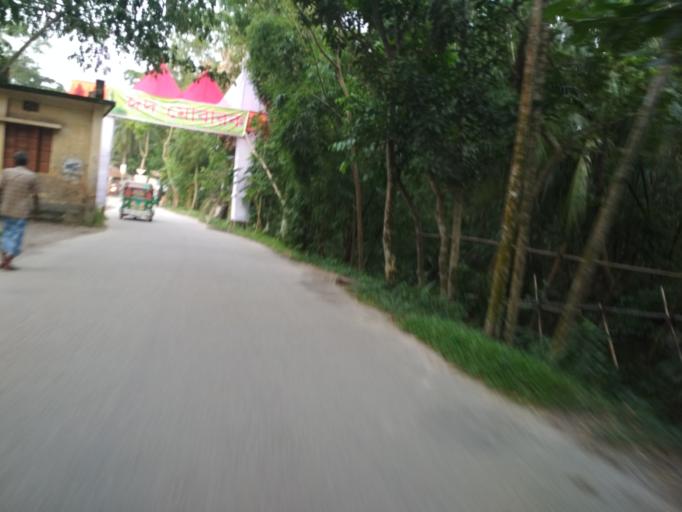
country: BD
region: Chittagong
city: Raipur
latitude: 23.0065
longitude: 90.7065
